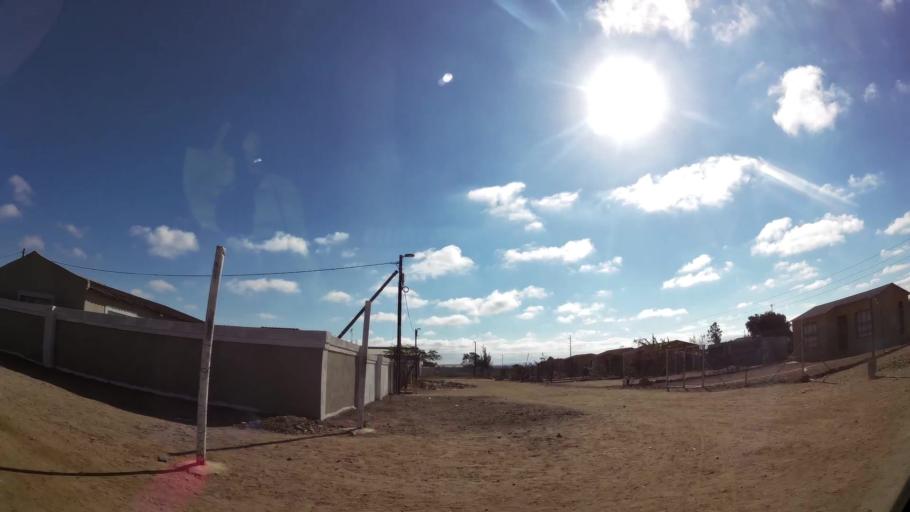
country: ZA
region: Limpopo
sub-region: Capricorn District Municipality
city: Polokwane
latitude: -23.8477
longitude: 29.4007
